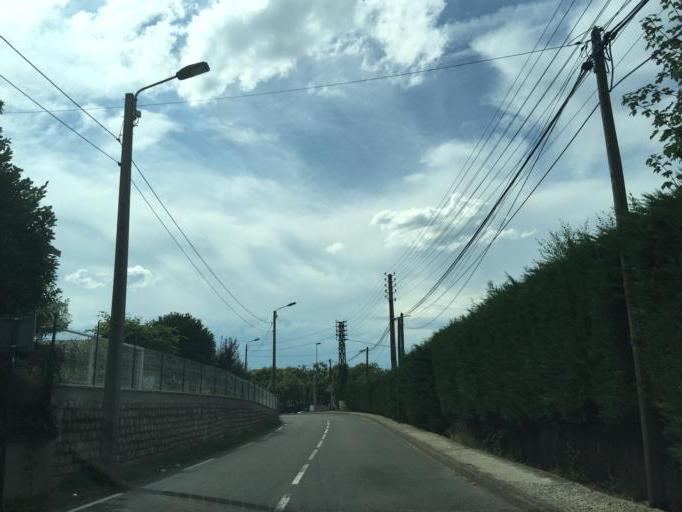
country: FR
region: Rhone-Alpes
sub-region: Departement de la Loire
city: Saint-Jean-Bonnefonds
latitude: 45.4400
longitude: 4.4300
